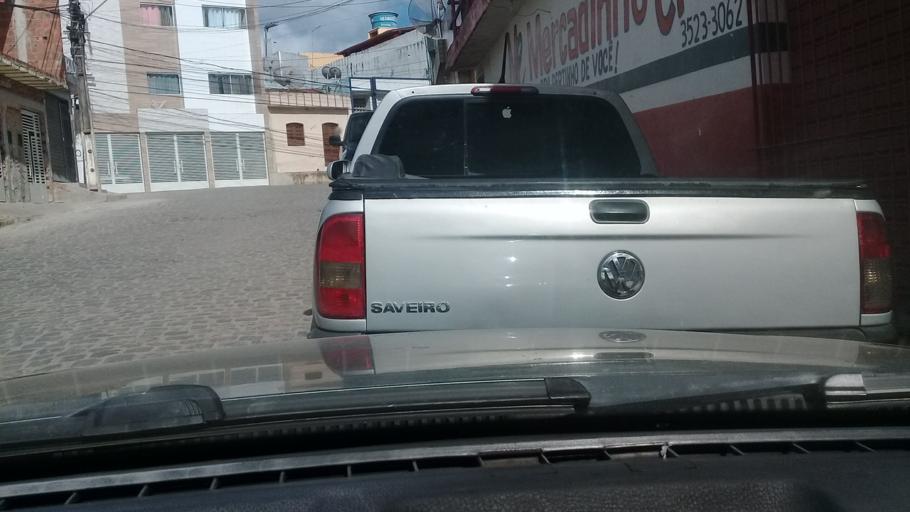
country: BR
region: Pernambuco
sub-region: Vitoria De Santo Antao
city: Vitoria de Santo Antao
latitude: -8.1248
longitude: -35.2971
